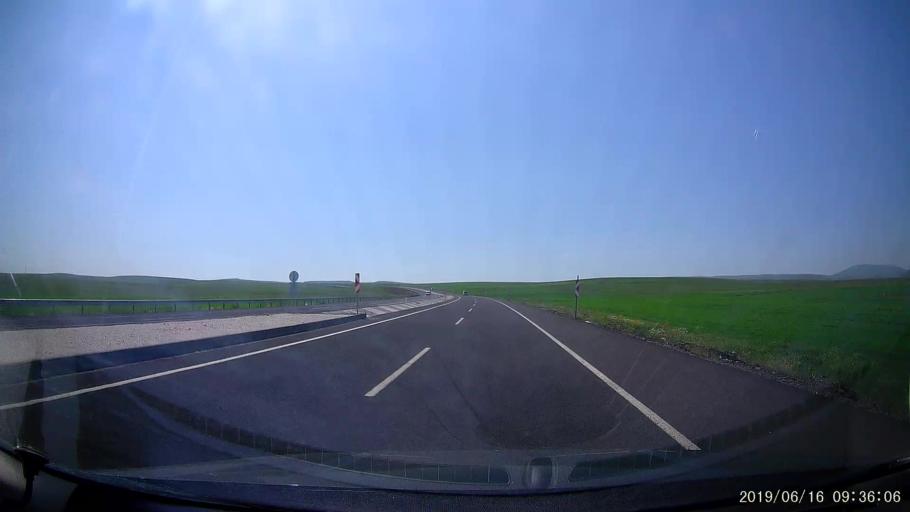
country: TR
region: Kars
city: Kars
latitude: 40.5618
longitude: 43.1665
